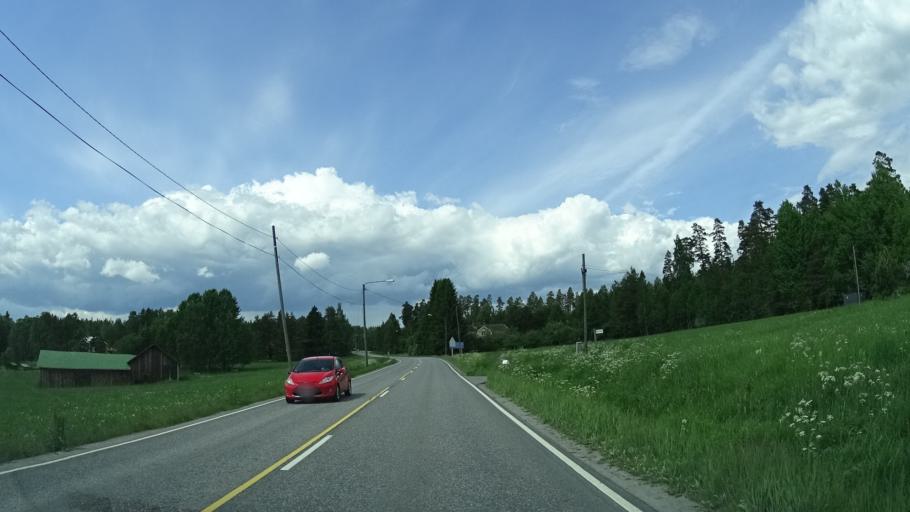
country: FI
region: Uusimaa
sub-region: Helsinki
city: Kirkkonummi
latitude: 60.2227
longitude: 24.4681
